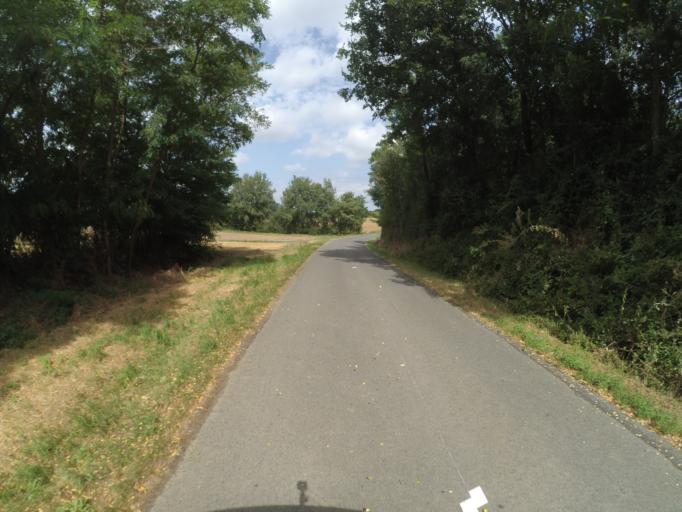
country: FR
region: Pays de la Loire
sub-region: Departement de Maine-et-Loire
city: Nueil-sur-Layon
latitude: 47.1802
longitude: -0.3507
